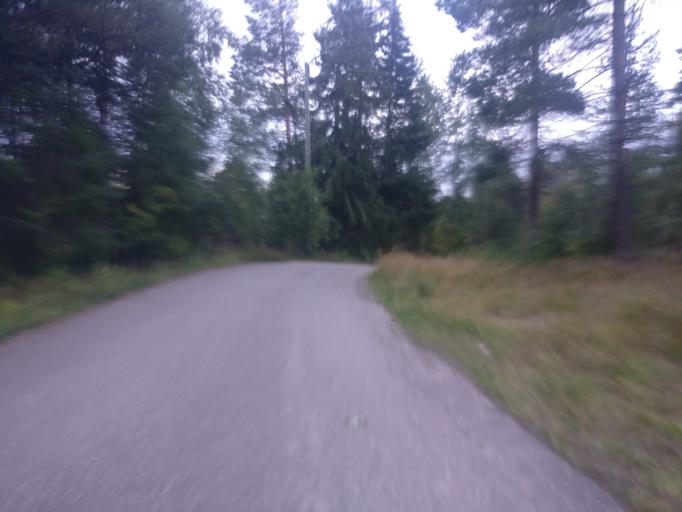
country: SE
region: Vaesternorrland
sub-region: Sundsvalls Kommun
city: Stockvik
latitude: 62.3657
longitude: 17.3706
